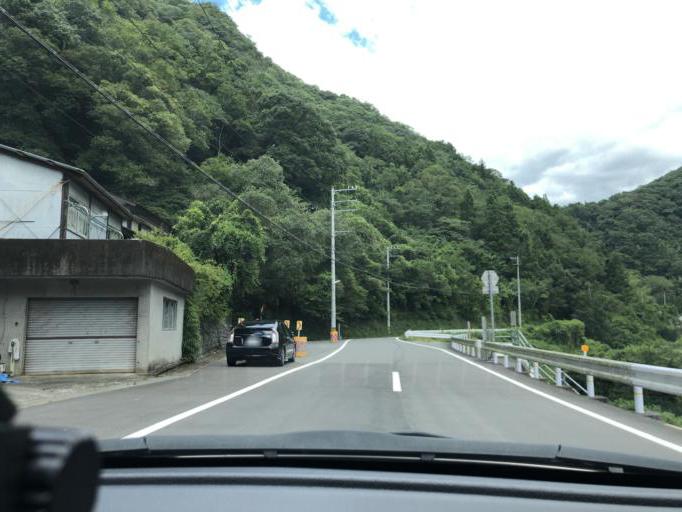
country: JP
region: Kochi
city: Kochi-shi
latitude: 33.6255
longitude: 133.4994
